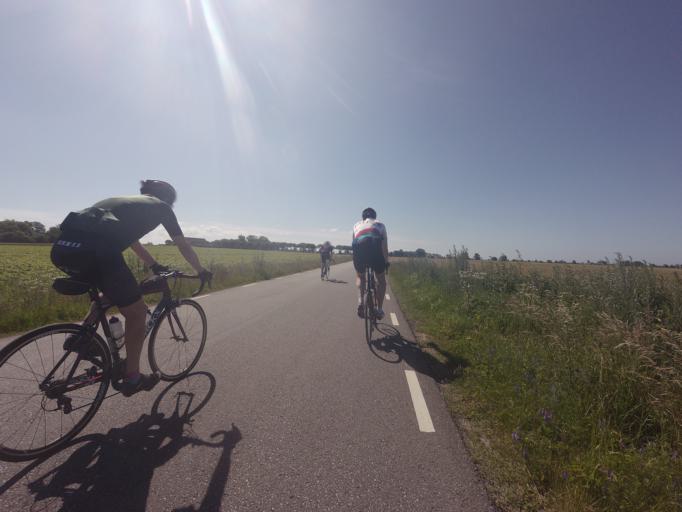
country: SE
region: Skane
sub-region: Malmo
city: Bunkeflostrand
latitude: 55.5164
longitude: 12.9349
